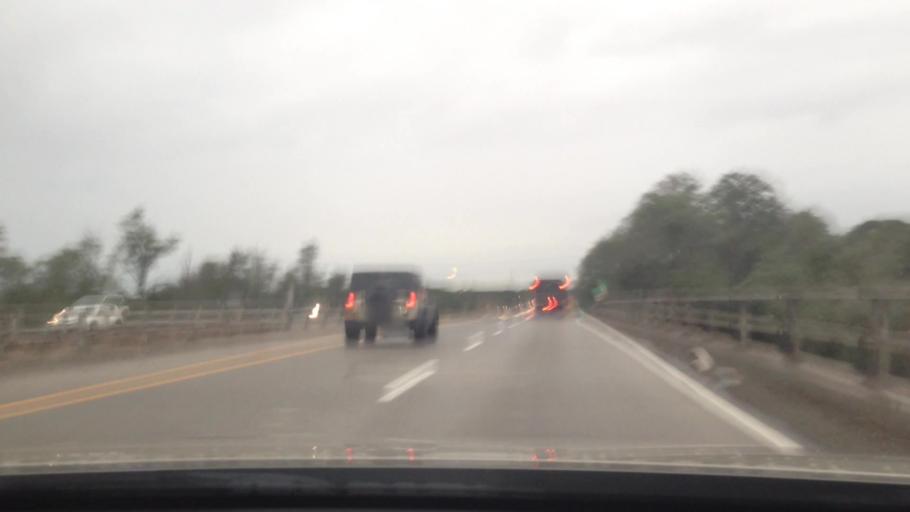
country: US
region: New York
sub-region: Suffolk County
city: Holtsville
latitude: 40.8126
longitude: -73.0530
